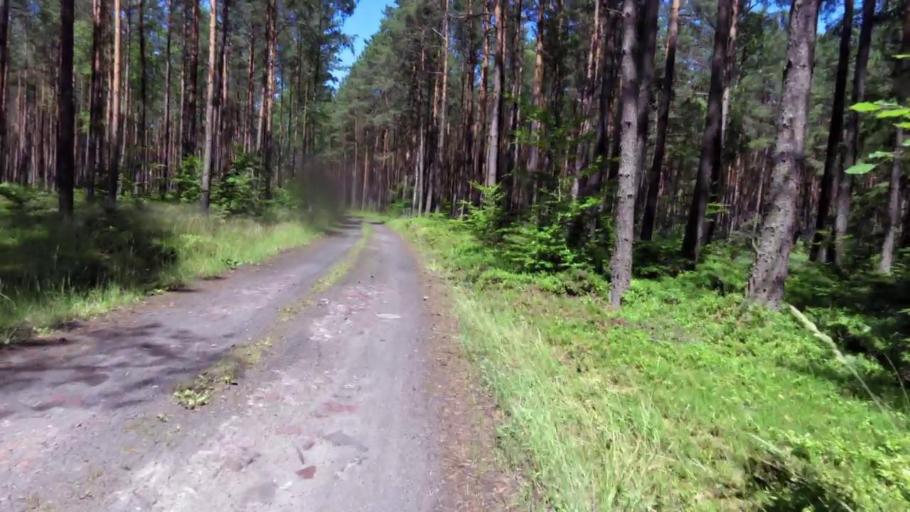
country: PL
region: West Pomeranian Voivodeship
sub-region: Powiat bialogardzki
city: Bialogard
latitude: 53.9481
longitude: 16.1144
